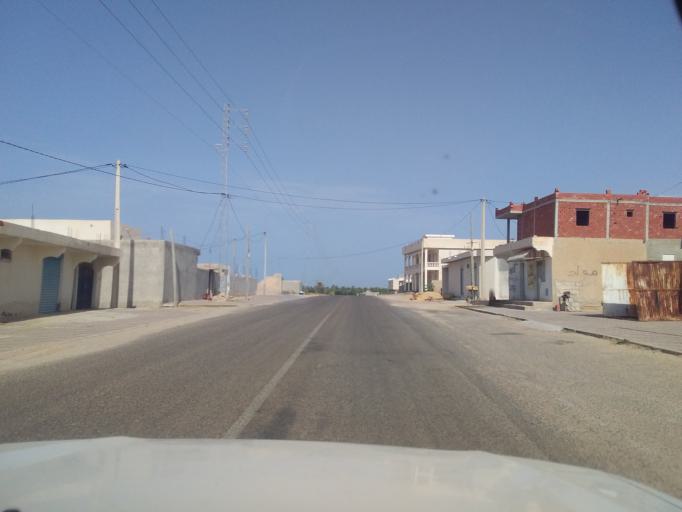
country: TN
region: Qabis
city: Gabes
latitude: 33.6420
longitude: 10.2952
